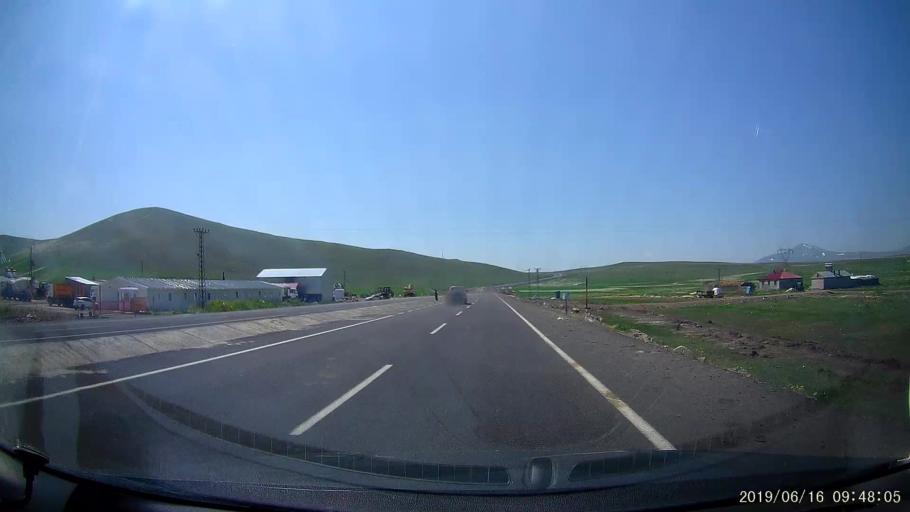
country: TR
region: Kars
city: Digor
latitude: 40.4374
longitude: 43.3507
